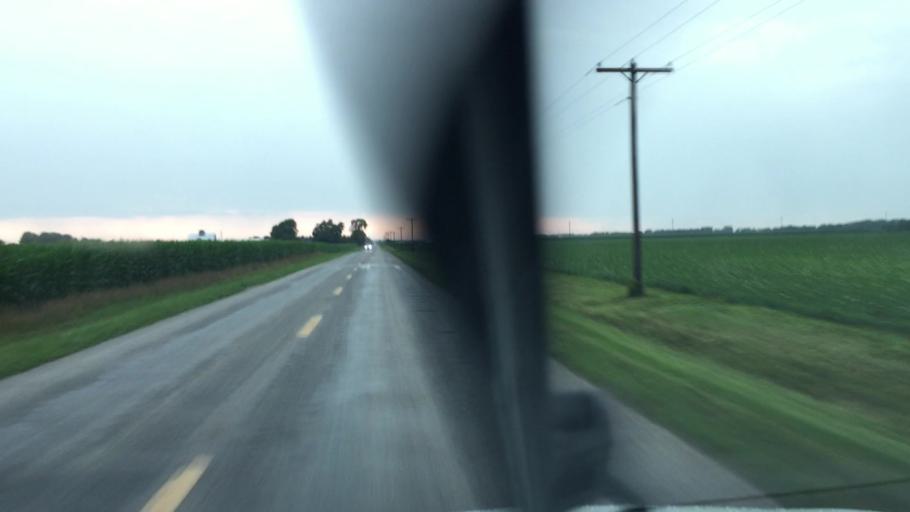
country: US
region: Iowa
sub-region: Lee County
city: Fort Madison
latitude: 40.5210
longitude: -91.2609
